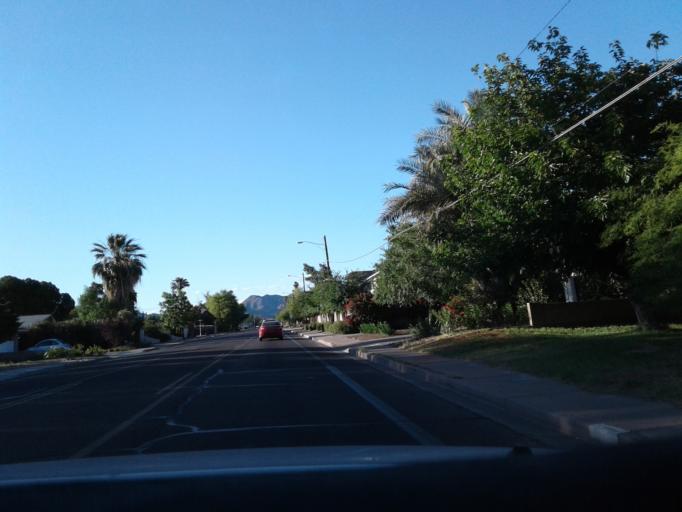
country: US
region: Arizona
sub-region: Maricopa County
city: Paradise Valley
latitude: 33.4903
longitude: -111.9954
